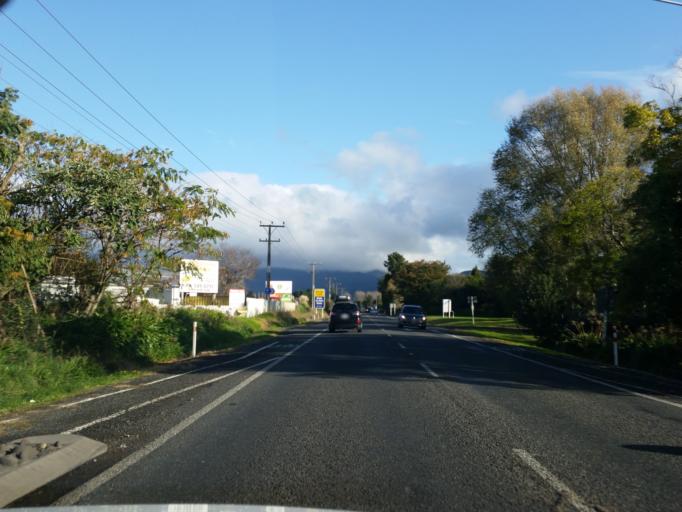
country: NZ
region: Bay of Plenty
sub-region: Western Bay of Plenty District
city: Katikati
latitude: -37.5626
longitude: 175.9142
